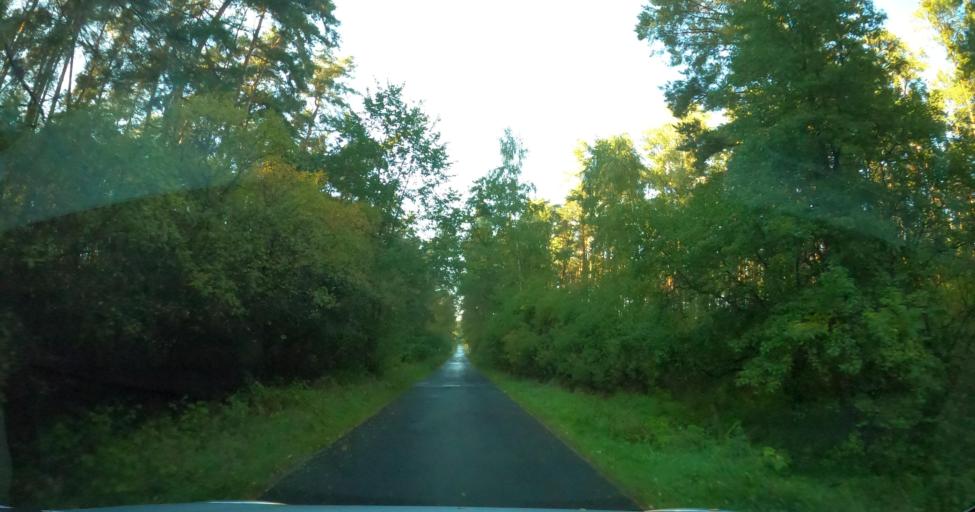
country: PL
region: Lubusz
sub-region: Powiat zielonogorski
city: Zabor
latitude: 51.9608
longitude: 15.6879
